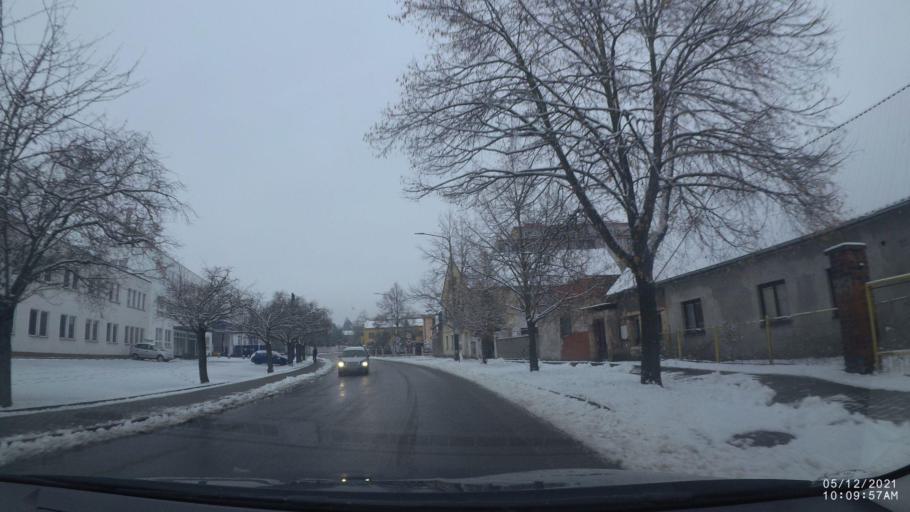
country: CZ
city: Kostelec nad Orlici
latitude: 50.1203
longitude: 16.2064
